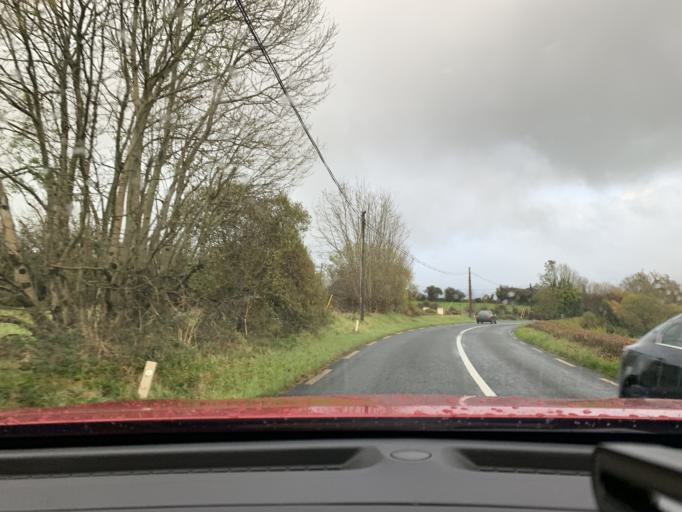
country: IE
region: Connaught
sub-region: Sligo
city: Ballymote
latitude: 54.0597
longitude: -8.5167
